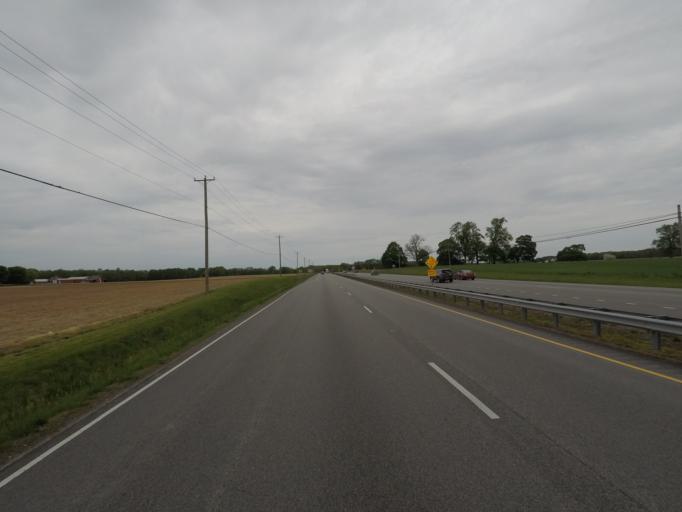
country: US
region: Maryland
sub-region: Queen Anne's County
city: Centreville
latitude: 38.9698
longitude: -76.1202
